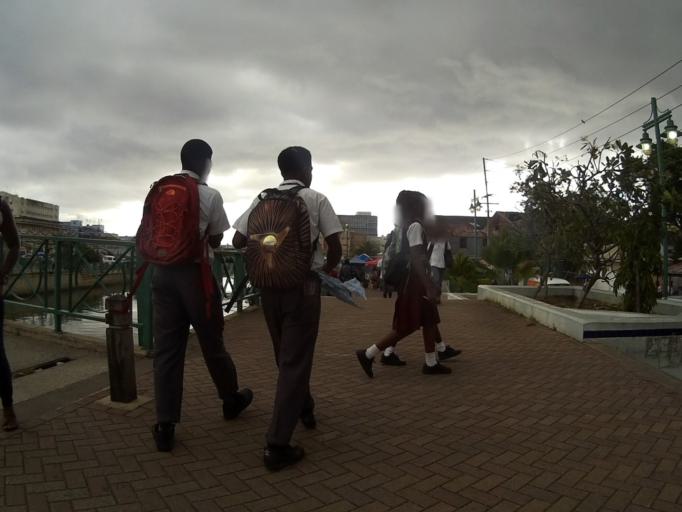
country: BB
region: Saint Michael
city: Bridgetown
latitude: 13.0972
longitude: -59.6105
